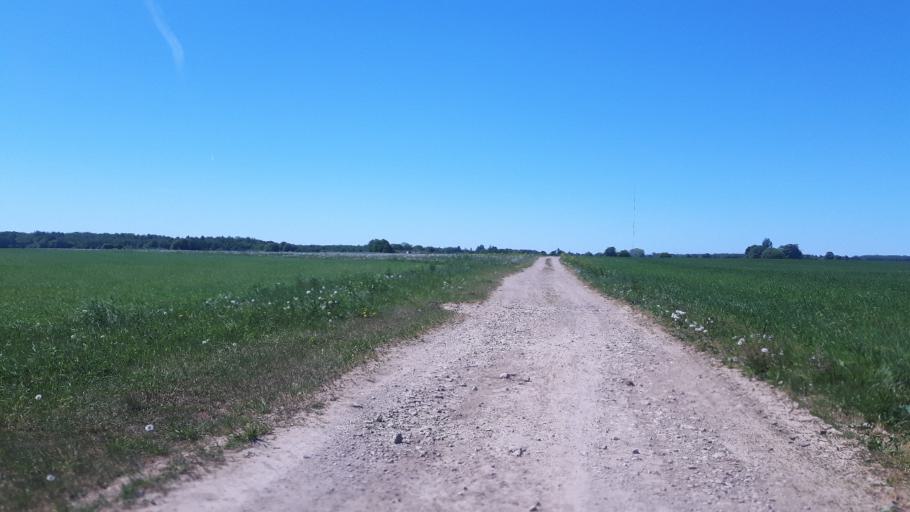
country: EE
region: Ida-Virumaa
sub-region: Toila vald
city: Voka
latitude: 59.4036
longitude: 27.6603
